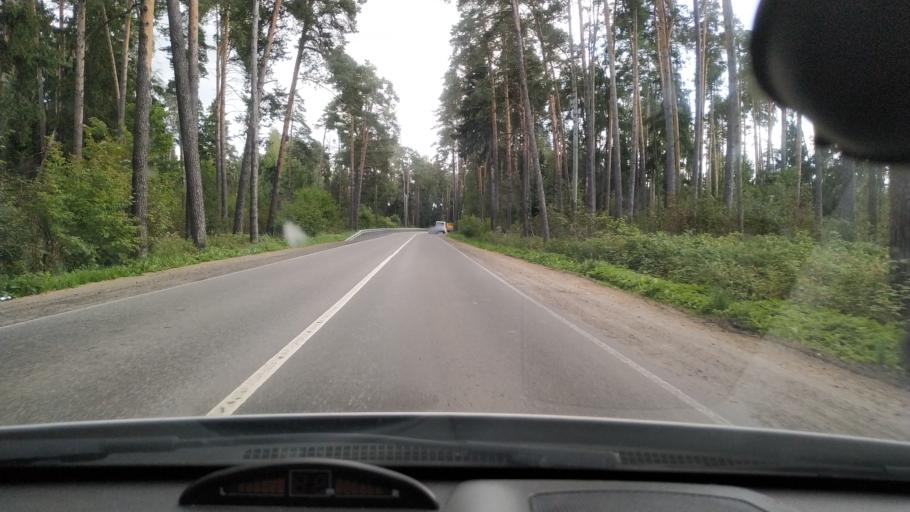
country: RU
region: Moskovskaya
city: Zheleznodorozhnyy
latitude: 55.7980
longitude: 38.0297
